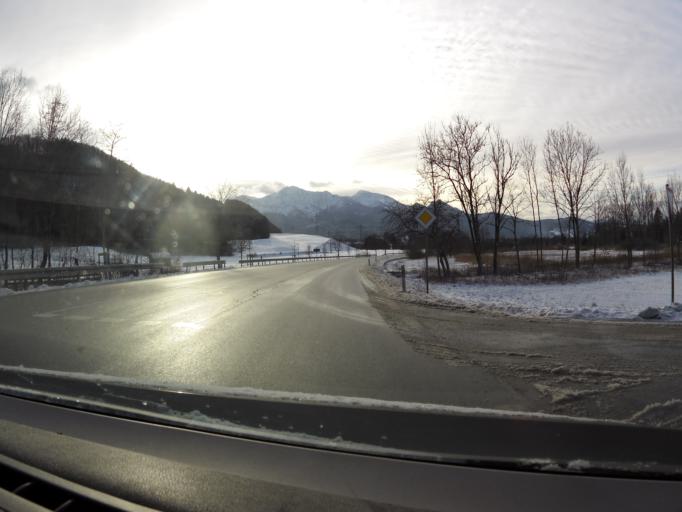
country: DE
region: Bavaria
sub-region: Upper Bavaria
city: Kochel
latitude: 47.6678
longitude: 11.3878
